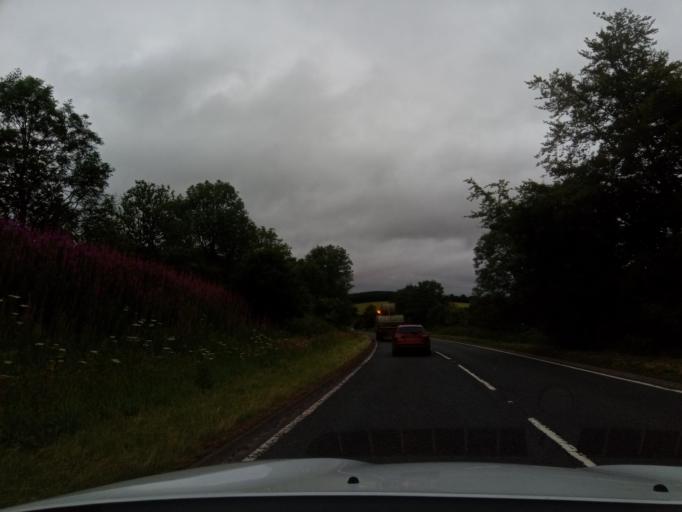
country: GB
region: Scotland
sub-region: The Scottish Borders
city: Lauder
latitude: 55.7661
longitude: -2.7823
